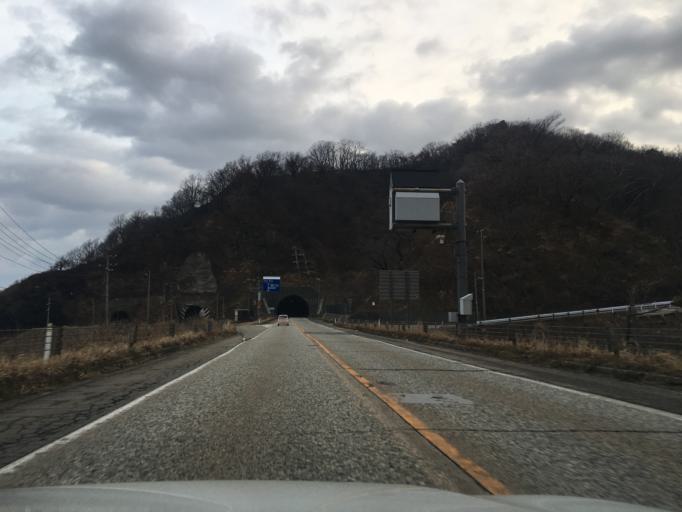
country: JP
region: Niigata
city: Murakami
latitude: 38.5062
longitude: 139.5244
